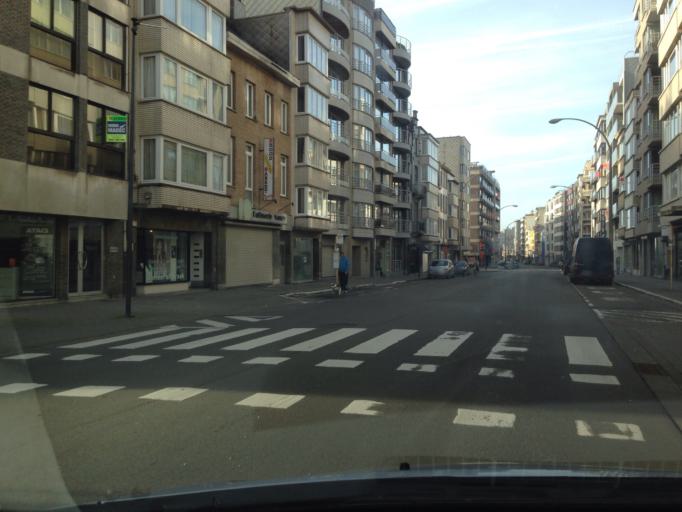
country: BE
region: Flanders
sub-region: Provincie West-Vlaanderen
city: Ostend
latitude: 51.2279
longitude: 2.9104
